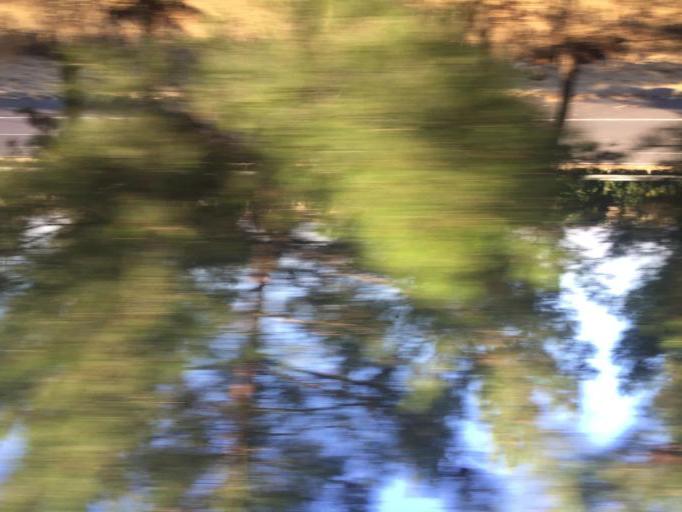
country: TR
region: Sanliurfa
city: Bogurtlen
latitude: 37.0999
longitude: 38.1943
